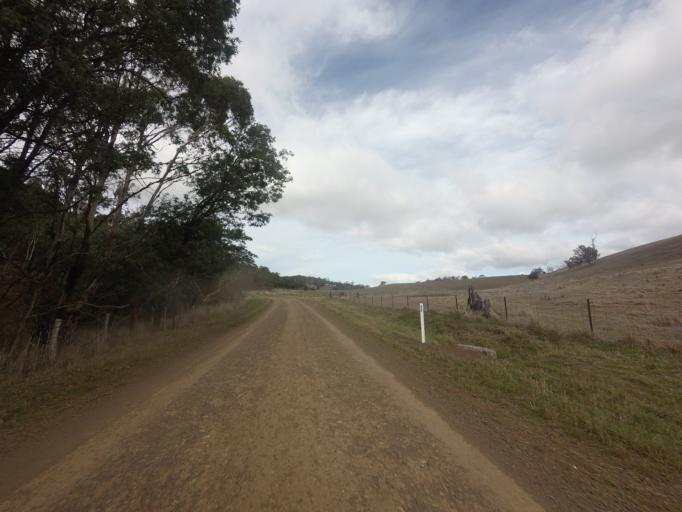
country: AU
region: Tasmania
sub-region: Brighton
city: Bridgewater
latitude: -42.4722
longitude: 147.2880
